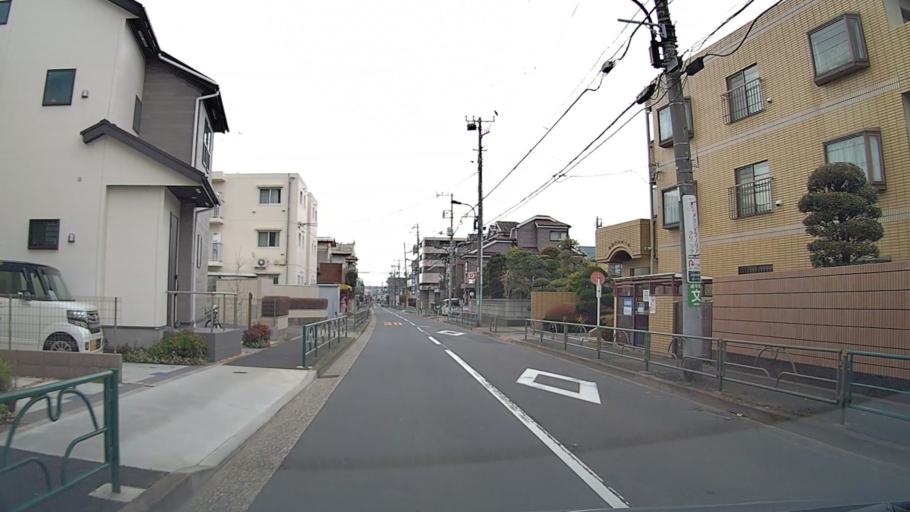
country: JP
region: Saitama
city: Wako
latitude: 35.7714
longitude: 139.5972
